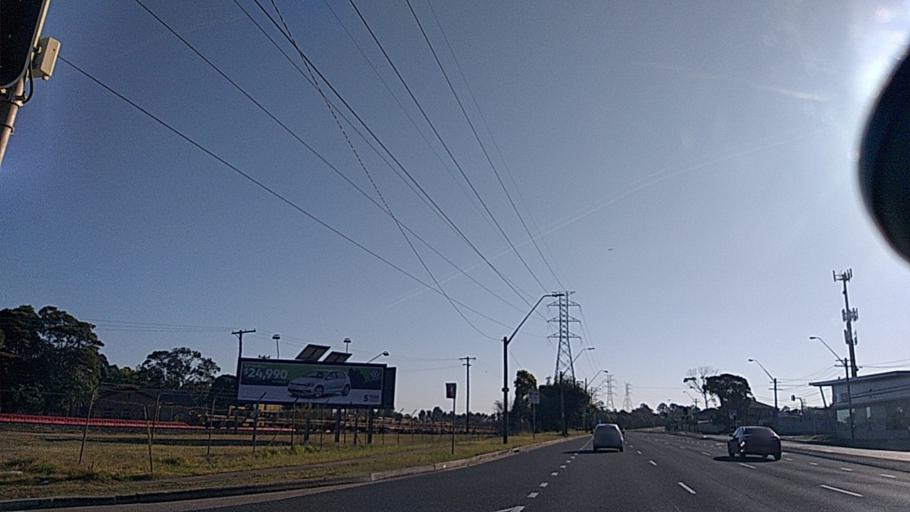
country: AU
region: New South Wales
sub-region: Strathfield
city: Strathfield South
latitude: -33.8904
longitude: 151.0589
